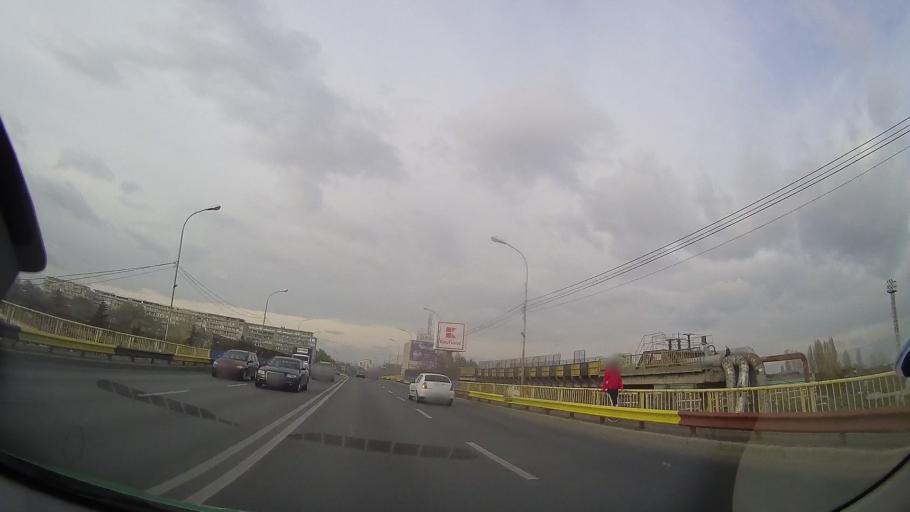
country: RO
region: Prahova
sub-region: Comuna Barcanesti
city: Tatarani
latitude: 44.9253
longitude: 26.0340
